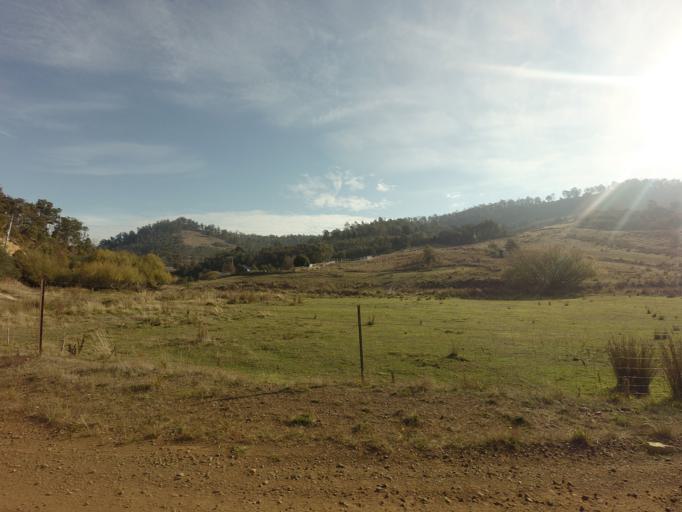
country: AU
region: Tasmania
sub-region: Sorell
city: Sorell
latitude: -42.5000
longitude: 147.4332
